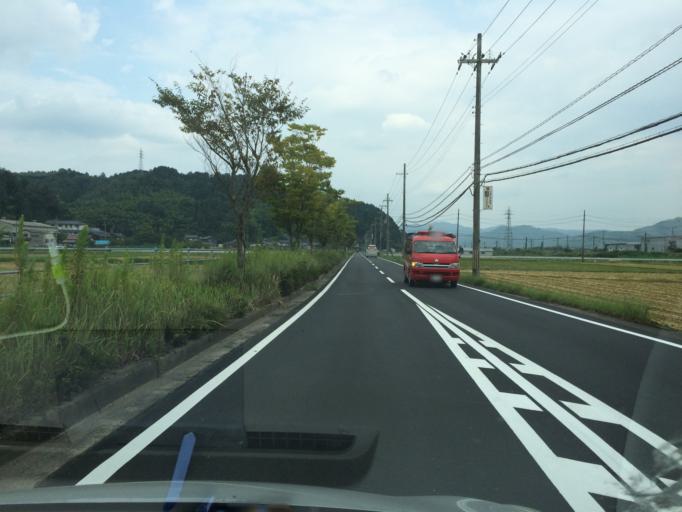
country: JP
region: Hyogo
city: Toyooka
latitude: 35.5086
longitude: 134.8117
